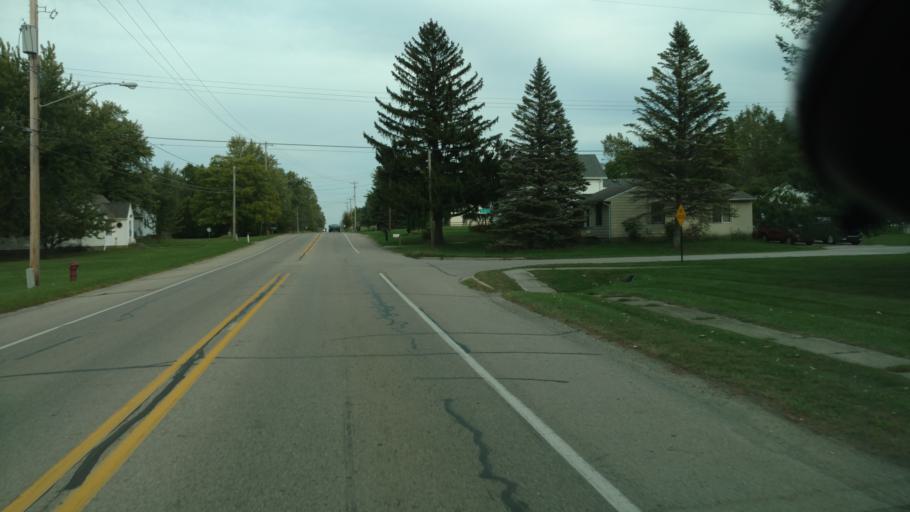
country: US
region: Michigan
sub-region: Ingham County
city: Lansing
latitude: 42.7842
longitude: -84.5354
